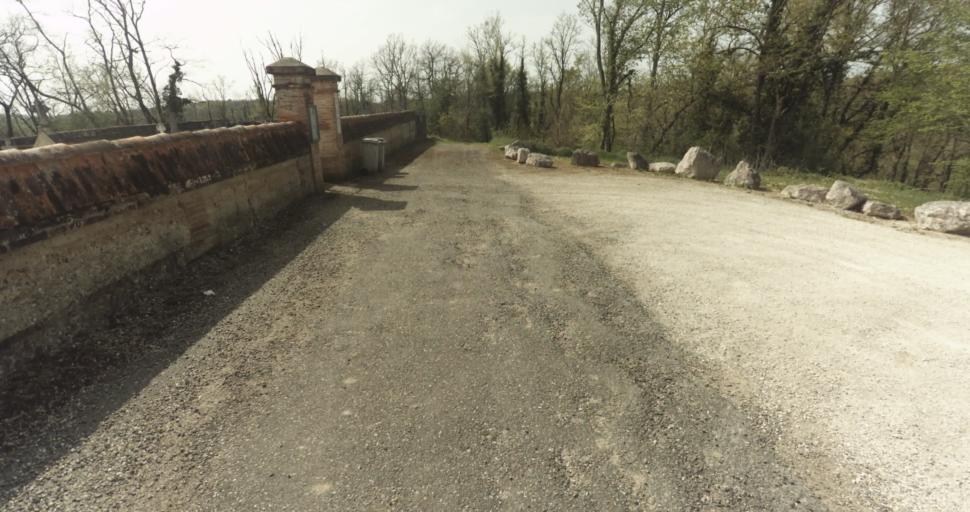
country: FR
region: Midi-Pyrenees
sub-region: Departement du Tarn-et-Garonne
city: Moissac
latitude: 44.1483
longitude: 1.1364
